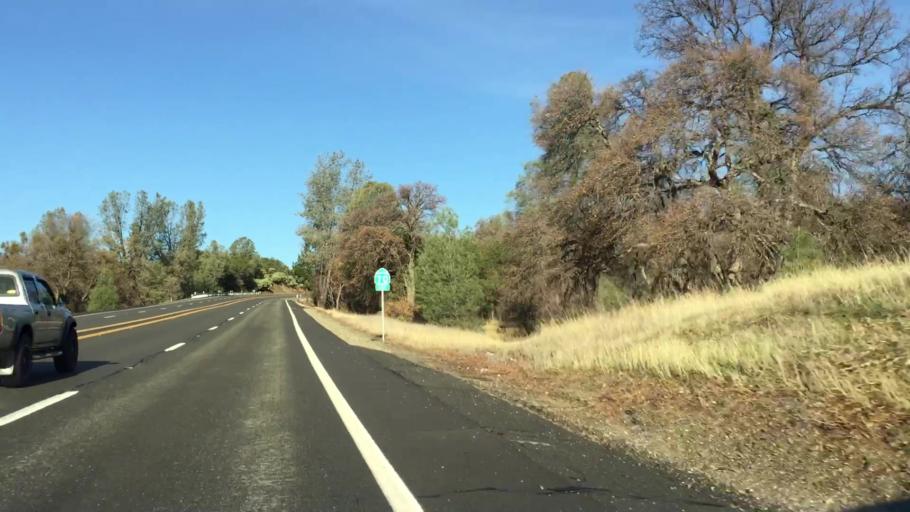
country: US
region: California
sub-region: Butte County
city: Paradise
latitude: 39.6775
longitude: -121.5447
